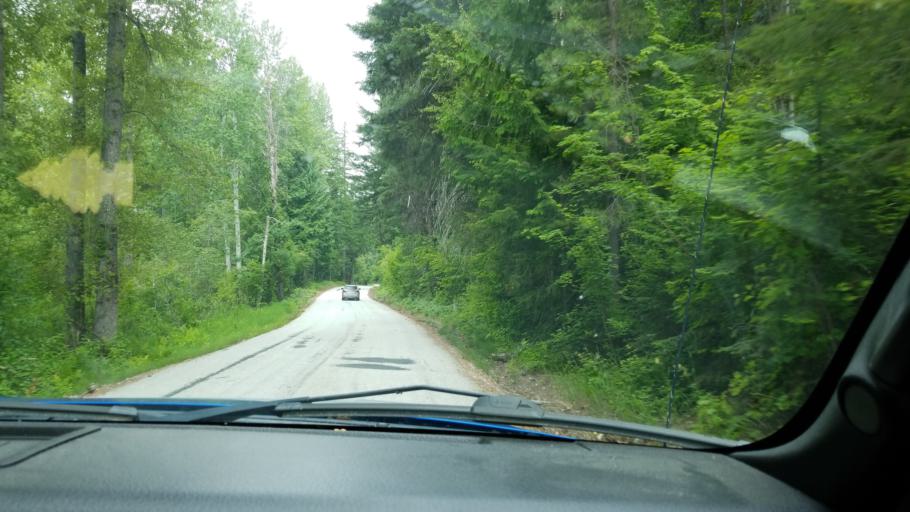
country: US
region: Washington
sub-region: Chelan County
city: Leavenworth
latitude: 47.8567
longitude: -120.8419
